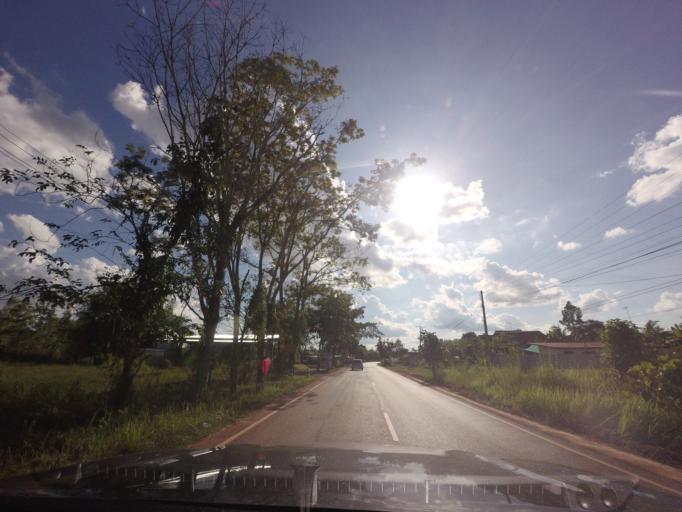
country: TH
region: Changwat Udon Thani
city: Ban Dung
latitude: 17.7436
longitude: 103.3142
